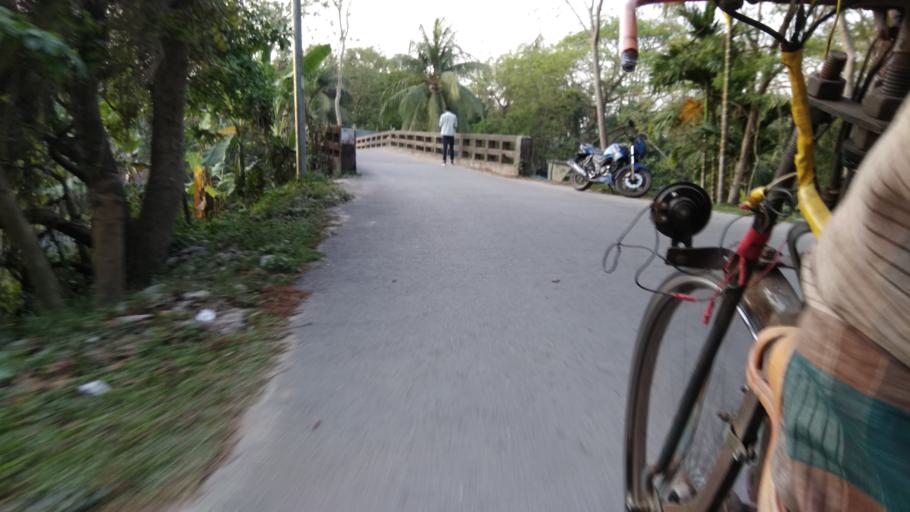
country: BD
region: Barisal
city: Mehendiganj
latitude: 22.9253
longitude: 90.4053
